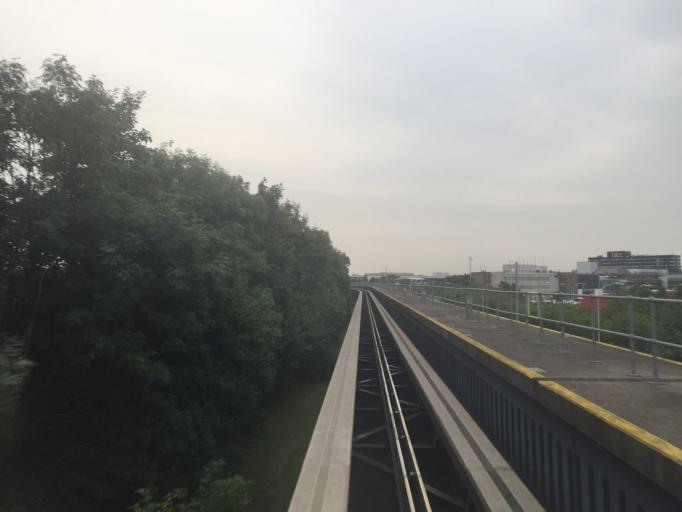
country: GB
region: England
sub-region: Surrey
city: Horley
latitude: 51.1609
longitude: -0.1680
